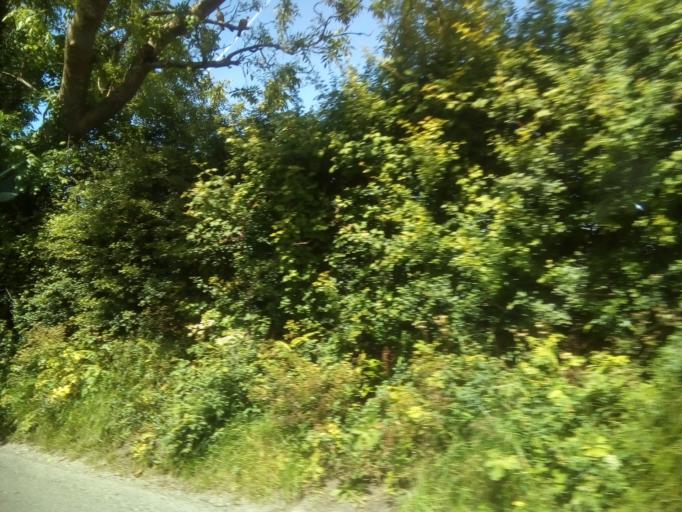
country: IE
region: Leinster
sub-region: Loch Garman
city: Loch Garman
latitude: 52.2357
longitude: -6.5851
